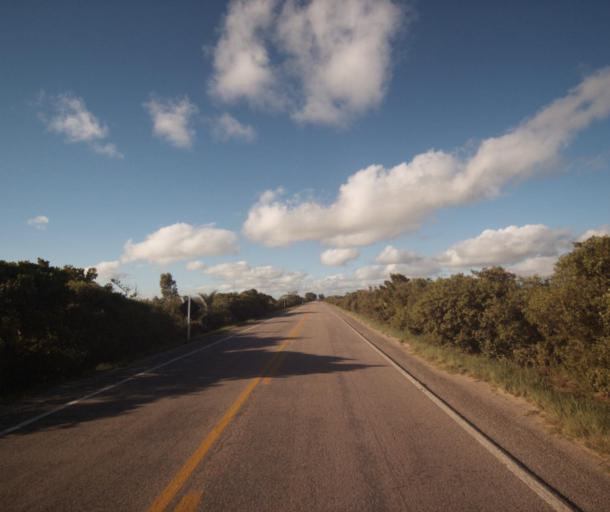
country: BR
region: Rio Grande do Sul
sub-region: Arroio Grande
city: Arroio Grande
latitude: -32.4901
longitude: -52.5802
